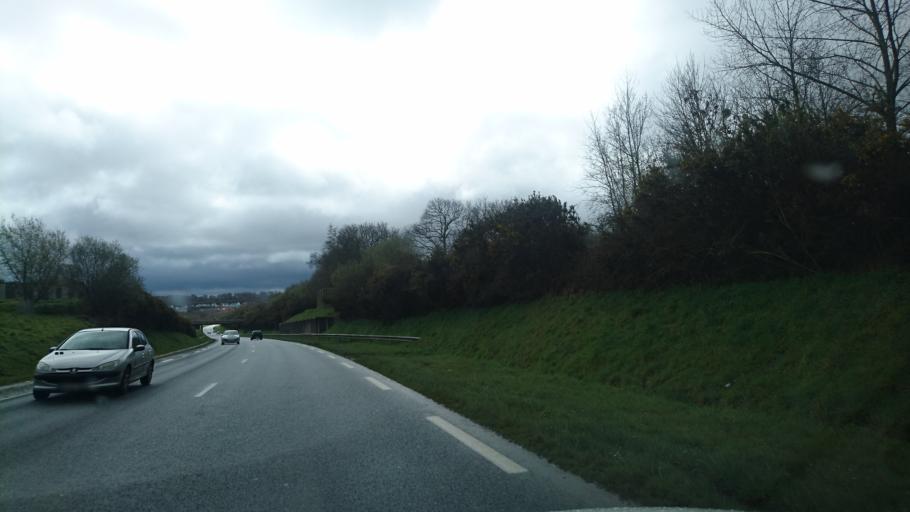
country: FR
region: Brittany
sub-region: Departement des Cotes-d'Armor
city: Lannion
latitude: 48.7450
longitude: -3.4453
